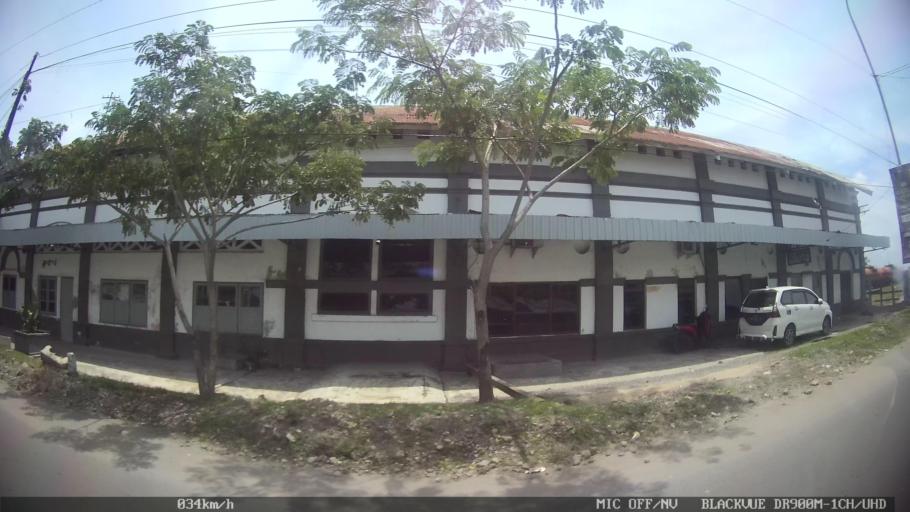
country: ID
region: North Sumatra
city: Belawan
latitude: 3.7804
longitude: 98.6817
